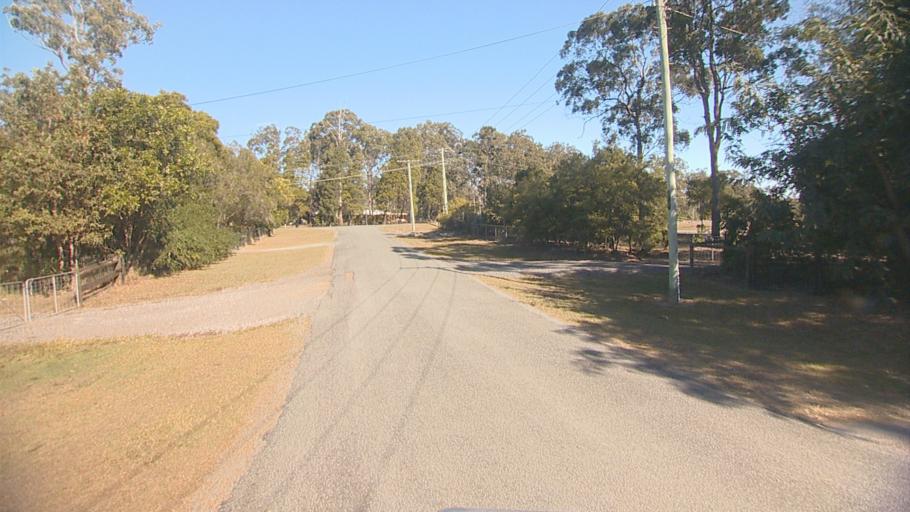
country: AU
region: Queensland
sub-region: Logan
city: Chambers Flat
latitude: -27.7785
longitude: 153.1089
